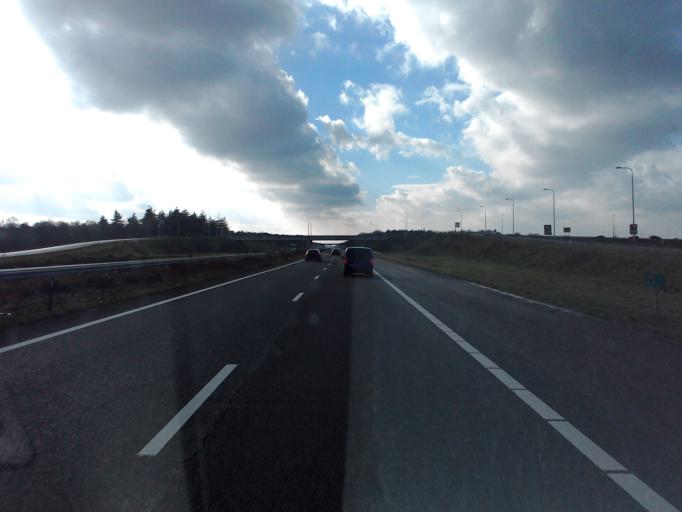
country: NL
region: North Brabant
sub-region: Gemeente Eersel
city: Eersel
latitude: 51.3527
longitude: 5.2776
